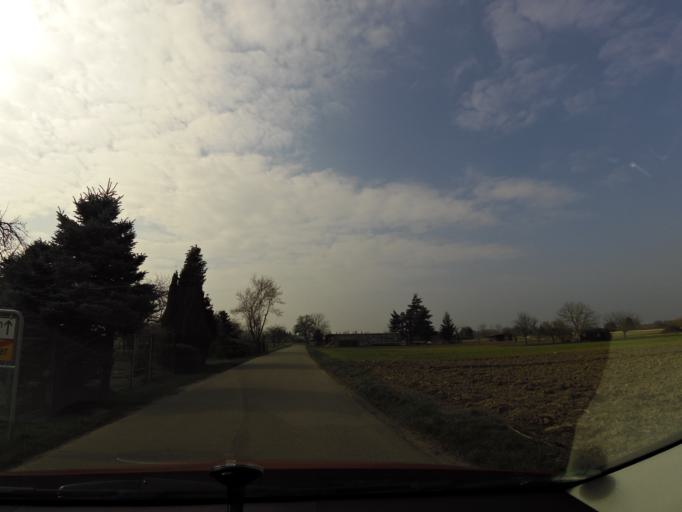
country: DE
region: Baden-Wuerttemberg
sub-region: Freiburg Region
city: Kehl
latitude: 48.5946
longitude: 7.8684
